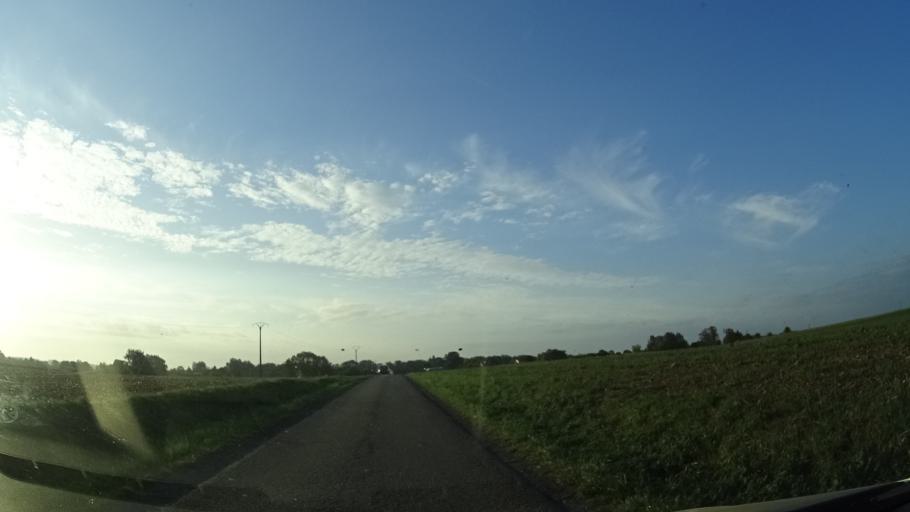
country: BE
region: Wallonia
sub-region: Province du Hainaut
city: Beaumont
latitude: 50.2536
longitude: 4.2536
